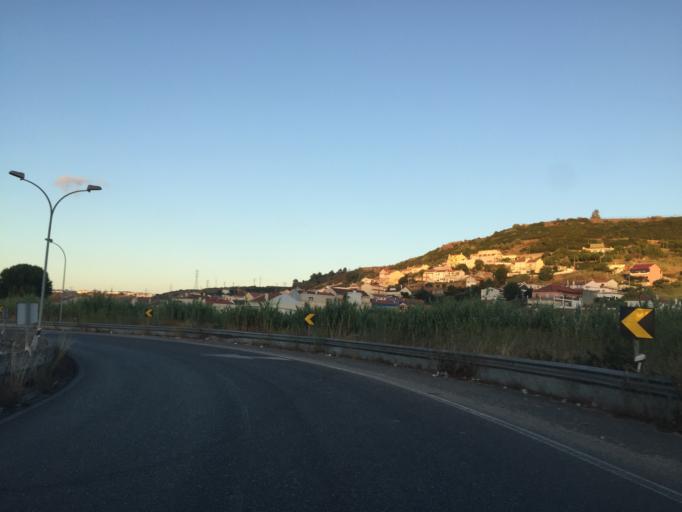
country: PT
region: Lisbon
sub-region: Odivelas
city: Odivelas
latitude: 38.7801
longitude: -9.1889
